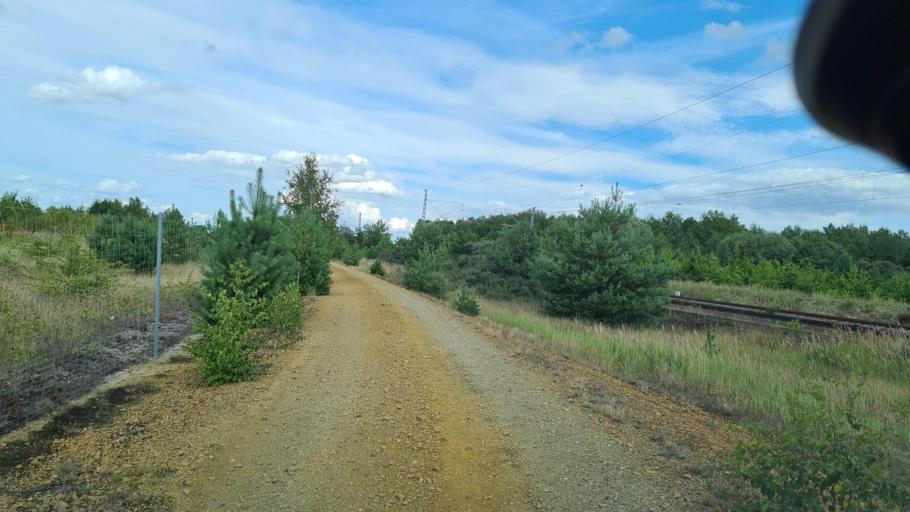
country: DE
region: Brandenburg
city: Spremberg
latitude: 51.5930
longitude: 14.3096
